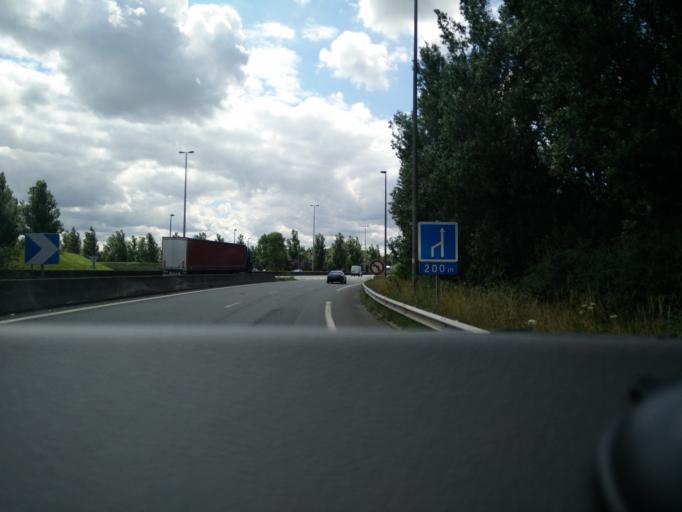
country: FR
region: Nord-Pas-de-Calais
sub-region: Departement du Nord
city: Coudekerque-Branche
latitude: 51.0211
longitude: 2.4098
